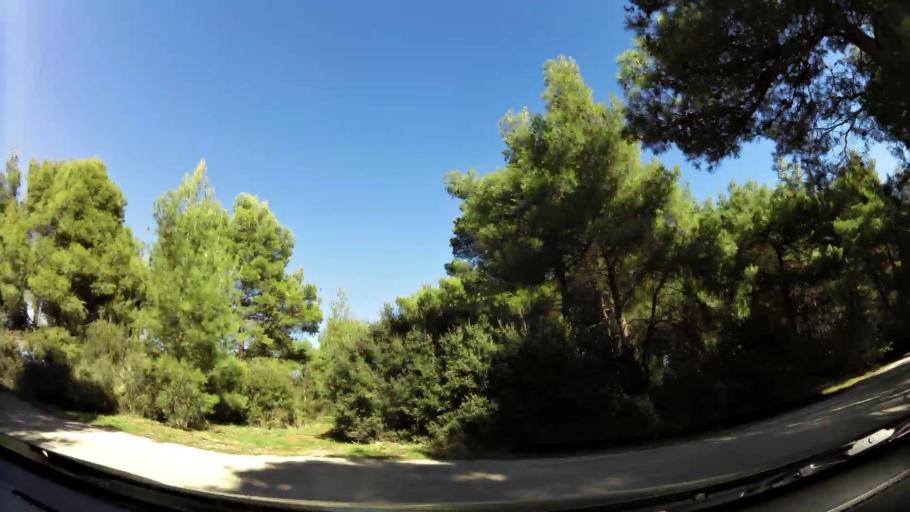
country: GR
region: Attica
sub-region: Nomarchia Anatolikis Attikis
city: Rodopoli
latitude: 38.1114
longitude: 23.8757
